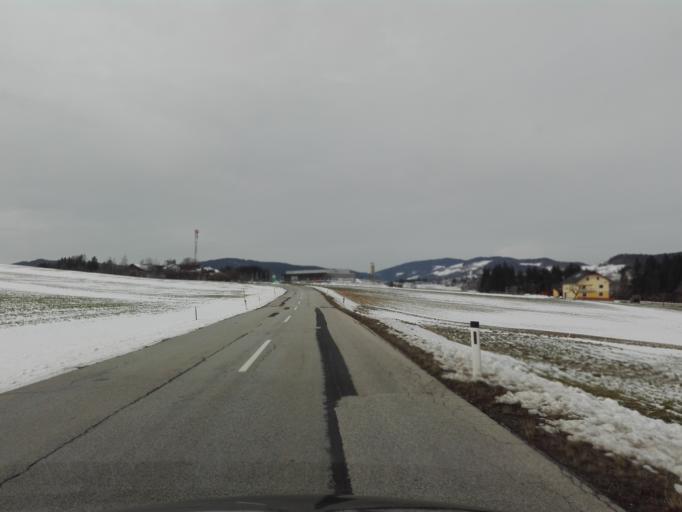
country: AT
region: Upper Austria
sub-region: Politischer Bezirk Rohrbach
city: Atzesberg
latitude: 48.5001
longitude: 13.8873
